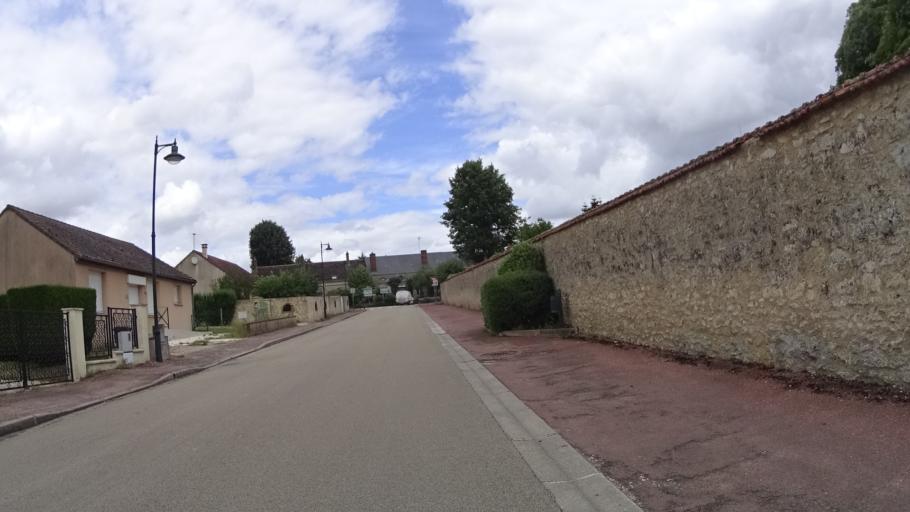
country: FR
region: Centre
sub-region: Departement du Loiret
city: Douchy
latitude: 47.9434
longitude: 3.0462
